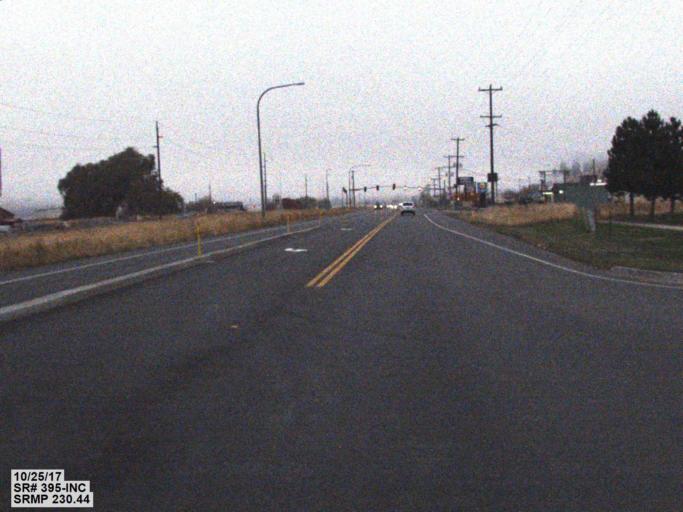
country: US
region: Washington
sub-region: Stevens County
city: Colville
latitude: 48.5532
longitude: -117.9179
